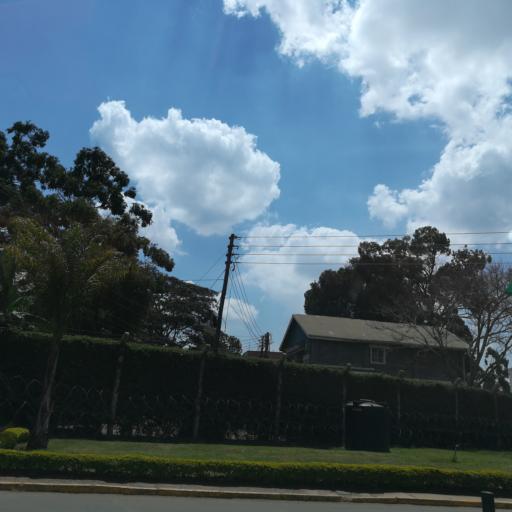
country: KE
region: Nairobi Area
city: Nairobi
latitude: -1.3178
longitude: 36.8142
